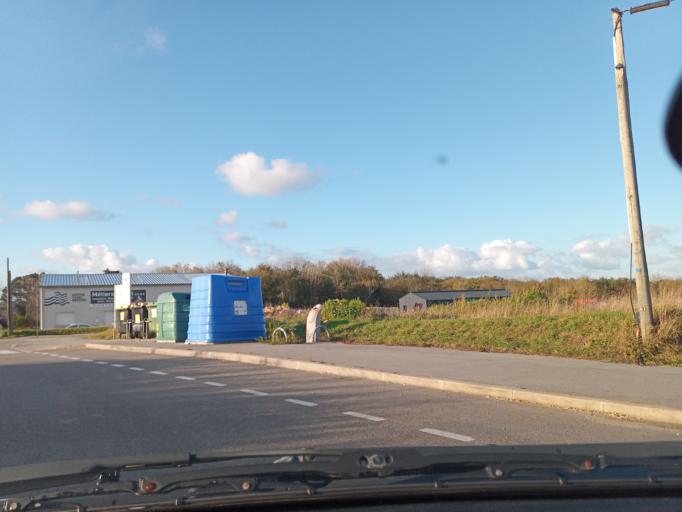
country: FR
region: Brittany
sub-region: Departement du Finistere
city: Esquibien
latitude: 48.0336
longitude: -4.5635
